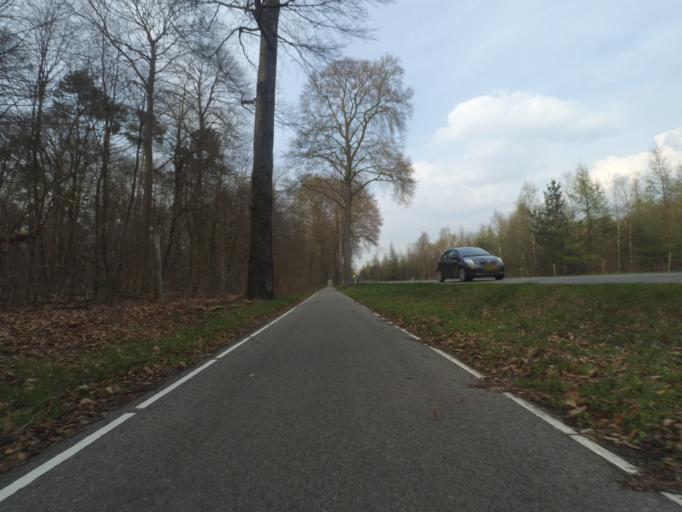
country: NL
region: Gelderland
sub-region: Gemeente Apeldoorn
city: Beekbergen
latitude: 52.1576
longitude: 5.8927
